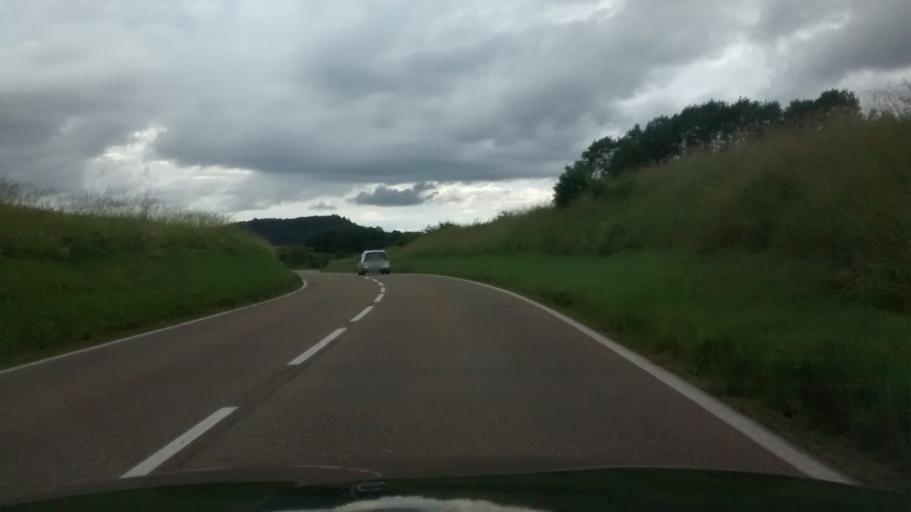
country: DE
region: Rheinland-Pfalz
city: Busenberg
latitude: 49.1251
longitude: 7.8409
